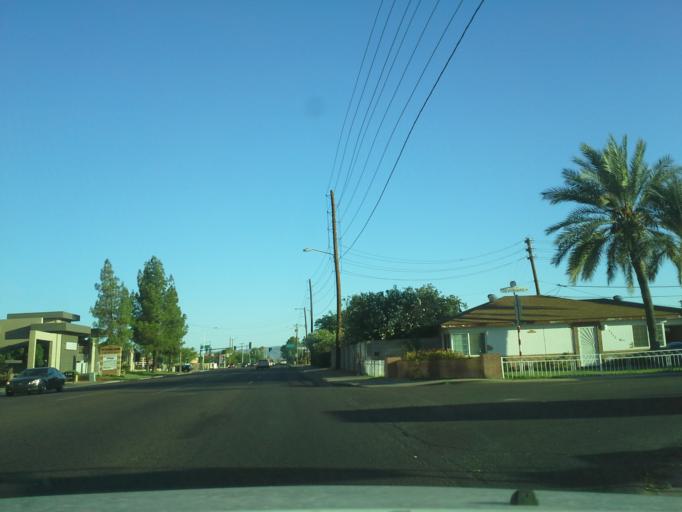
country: US
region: Arizona
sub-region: Maricopa County
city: Phoenix
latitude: 33.4968
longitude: -112.0303
